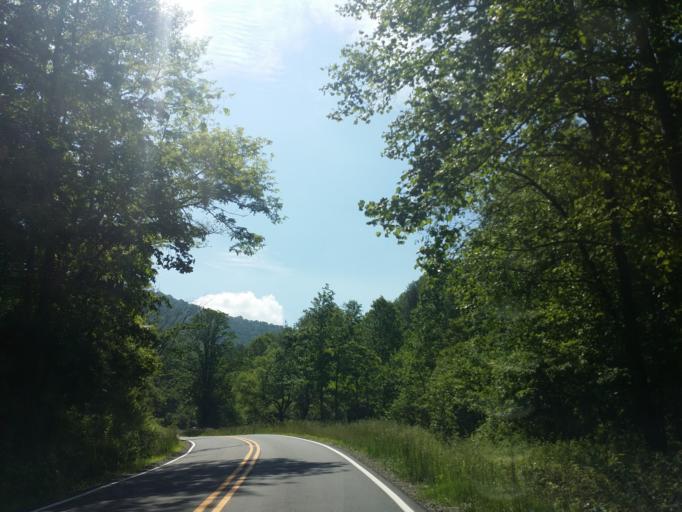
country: US
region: North Carolina
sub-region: Madison County
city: Marshall
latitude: 35.7496
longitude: -82.8661
